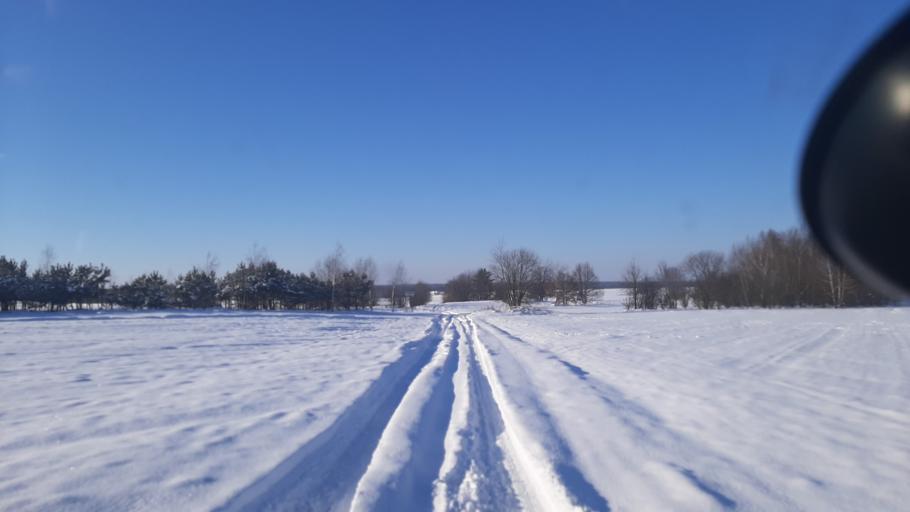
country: PL
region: Lublin Voivodeship
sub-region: Powiat lubelski
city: Jastkow
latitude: 51.3774
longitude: 22.4363
